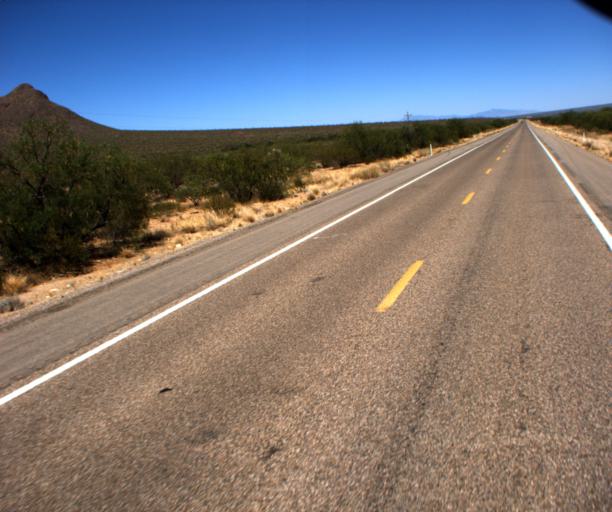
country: US
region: Arizona
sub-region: Pima County
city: Three Points
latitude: 32.0409
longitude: -111.4599
